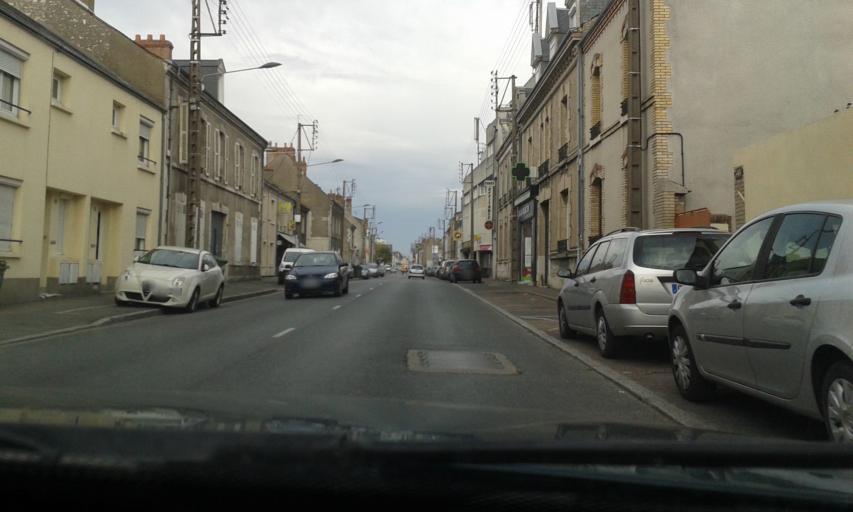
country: FR
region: Centre
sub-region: Departement du Loiret
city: Fleury-les-Aubrais
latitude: 47.9294
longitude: 1.8959
